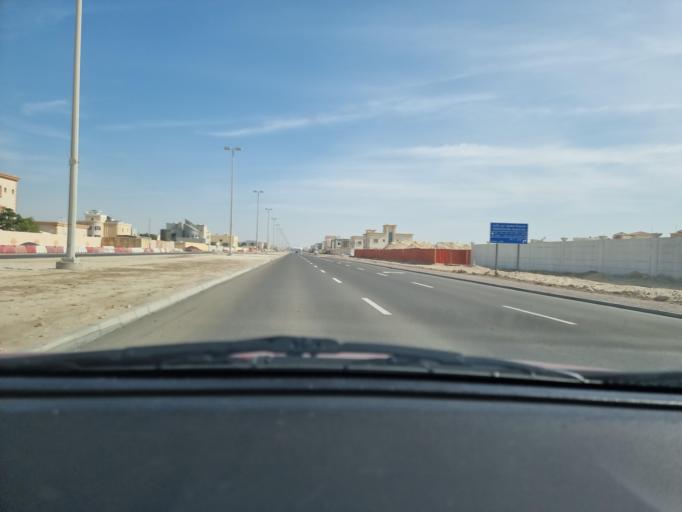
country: AE
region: Abu Dhabi
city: Abu Dhabi
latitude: 24.3161
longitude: 54.5642
